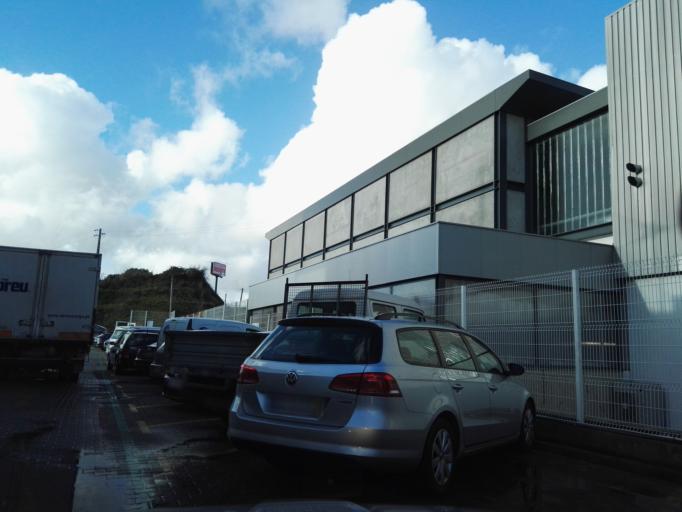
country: PT
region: Lisbon
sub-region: Amadora
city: Amadora
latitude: 38.7406
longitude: -9.2260
